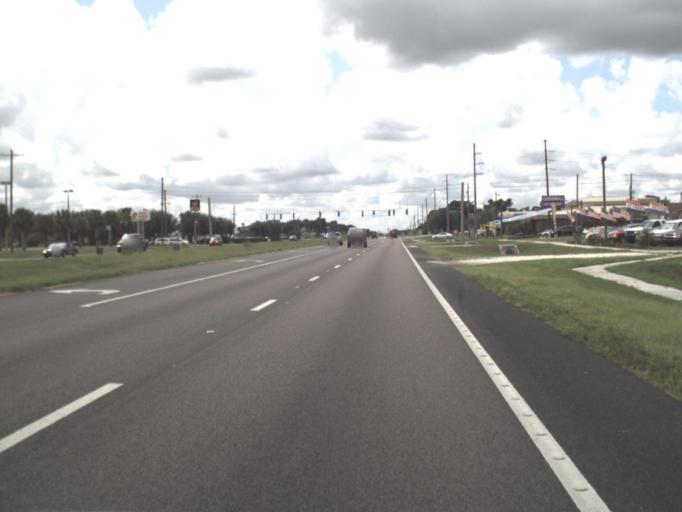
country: US
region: Florida
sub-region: Hardee County
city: Wauchula
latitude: 27.5713
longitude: -81.8166
